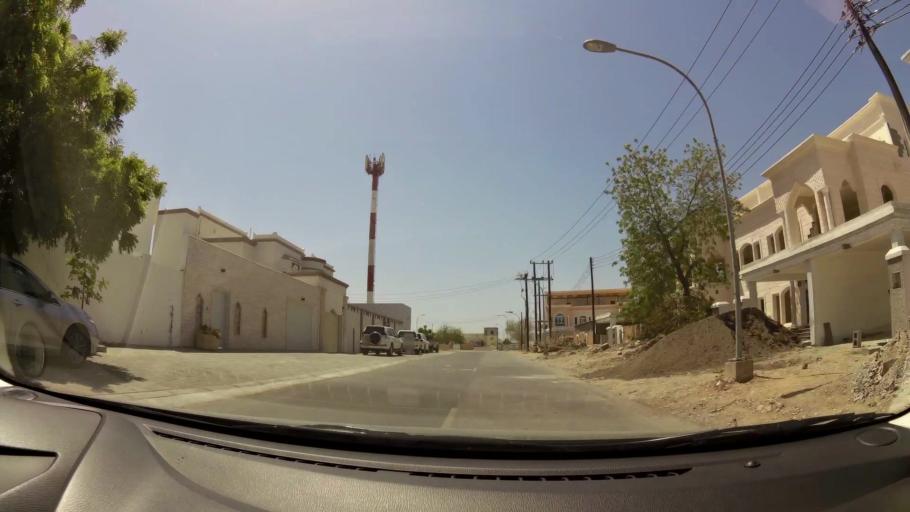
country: OM
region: Muhafazat Masqat
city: As Sib al Jadidah
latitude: 23.6300
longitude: 58.2274
